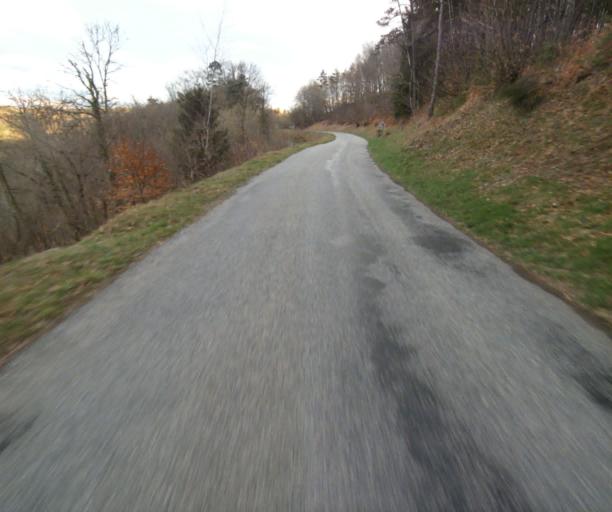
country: FR
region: Limousin
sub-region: Departement de la Correze
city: Argentat
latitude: 45.2503
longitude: 1.9838
